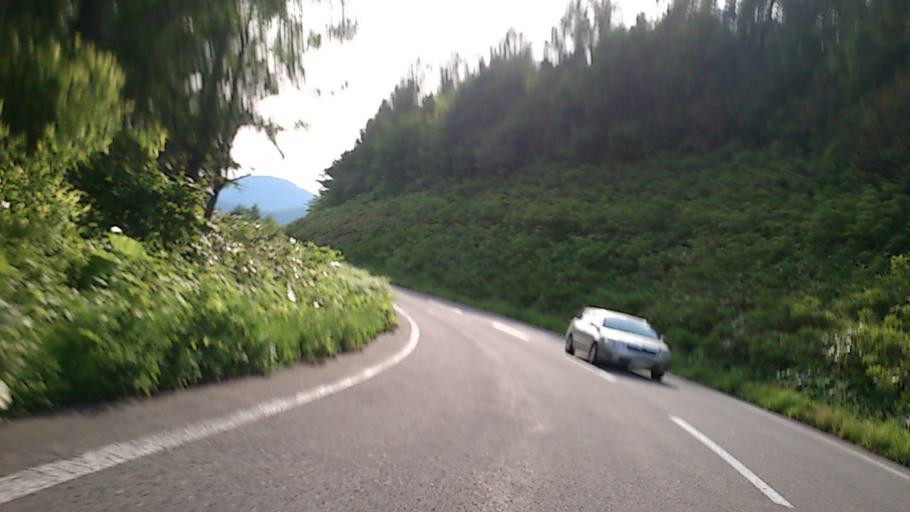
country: JP
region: Aomori
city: Aomori Shi
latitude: 40.6486
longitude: 140.7795
